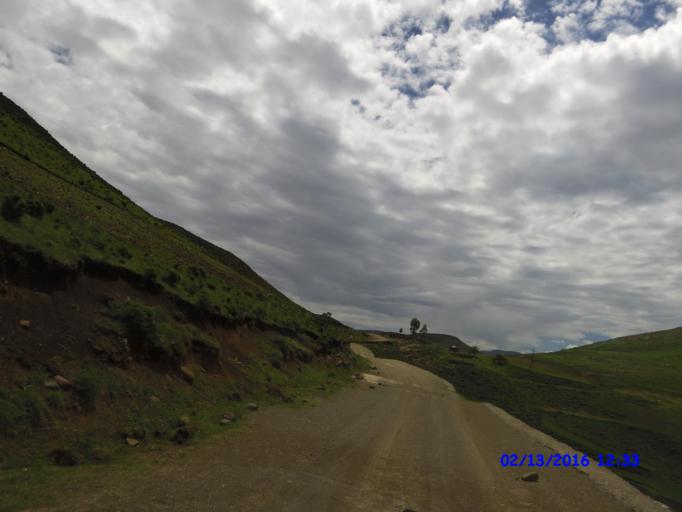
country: LS
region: Maseru
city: Nako
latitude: -29.8499
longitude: 28.0283
